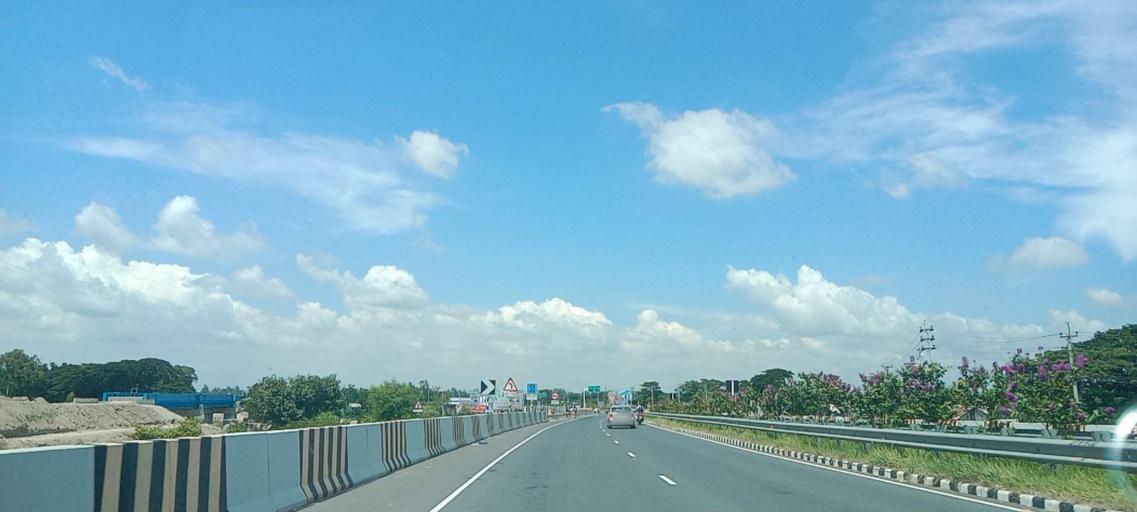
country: BD
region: Dhaka
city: Dohar
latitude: 23.5262
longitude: 90.2865
